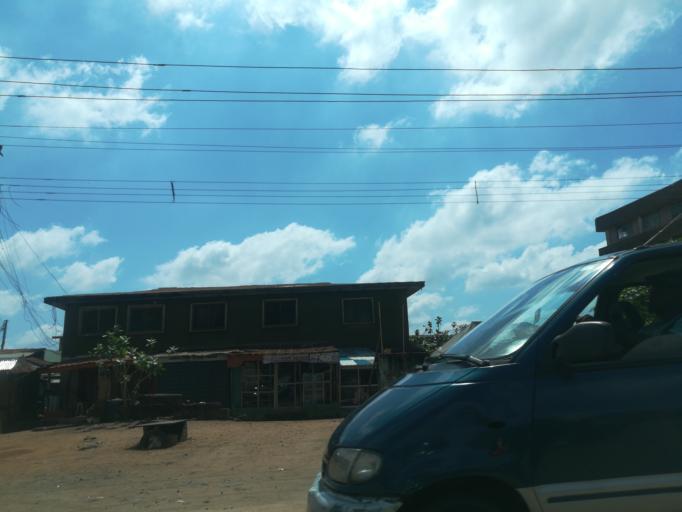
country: NG
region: Oyo
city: Ibadan
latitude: 7.3575
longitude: 3.8678
